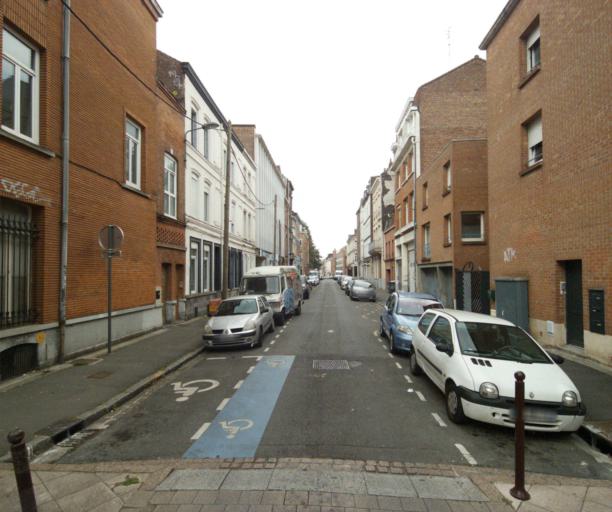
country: FR
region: Nord-Pas-de-Calais
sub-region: Departement du Nord
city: Lille
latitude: 50.6286
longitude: 3.0524
